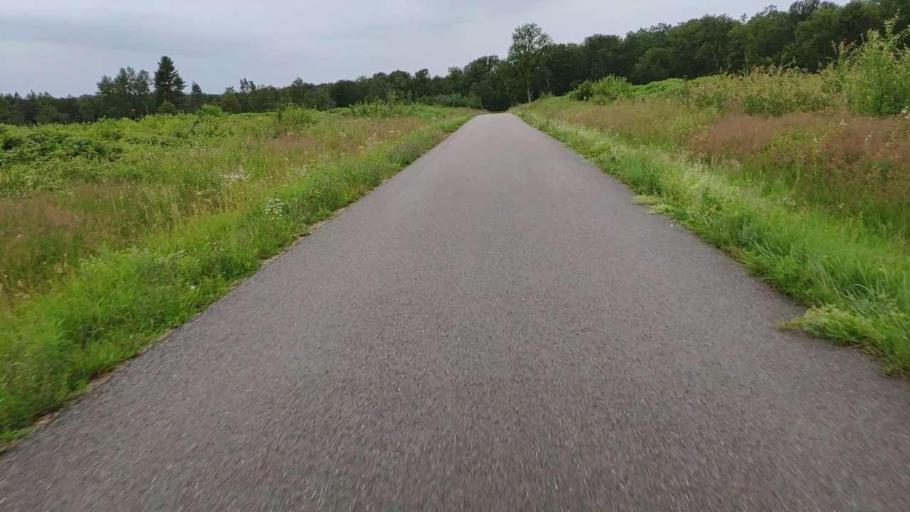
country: FR
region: Franche-Comte
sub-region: Departement du Jura
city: Chaussin
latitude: 46.8967
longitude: 5.4334
